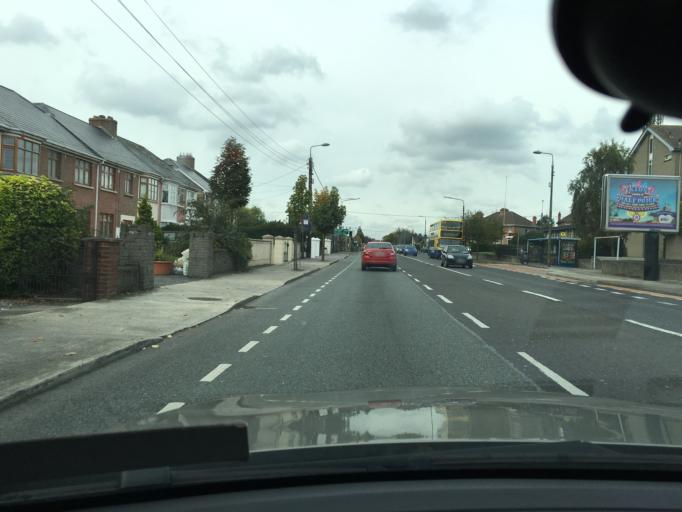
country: IE
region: Leinster
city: Cabra
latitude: 53.3644
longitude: -6.3068
